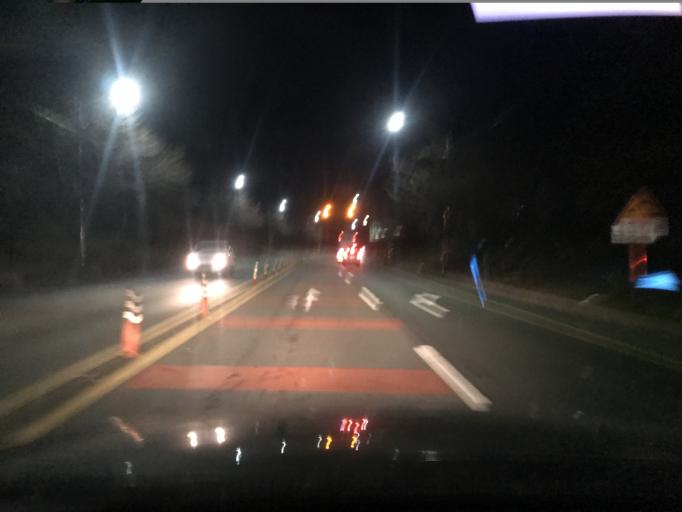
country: KR
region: Daegu
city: Hwawon
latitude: 35.7296
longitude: 128.4678
